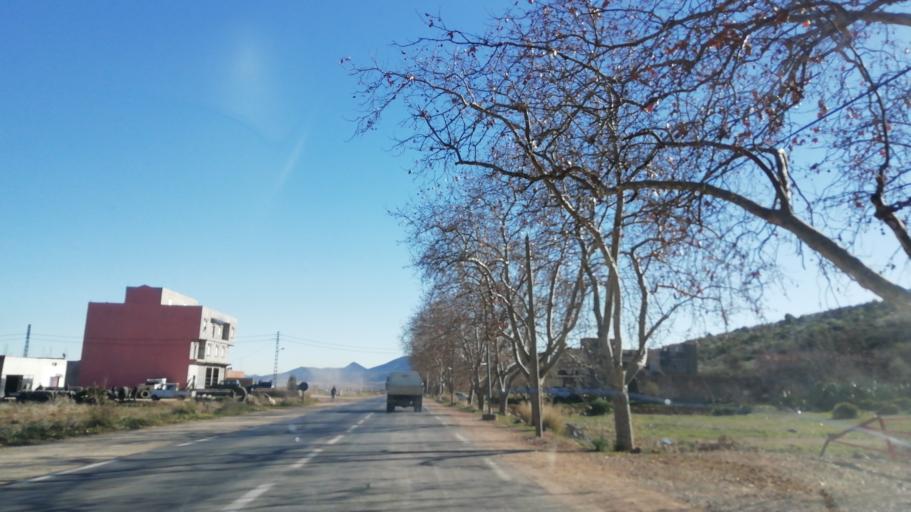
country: DZ
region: Tlemcen
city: Chetouane
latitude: 34.8678
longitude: -1.1797
